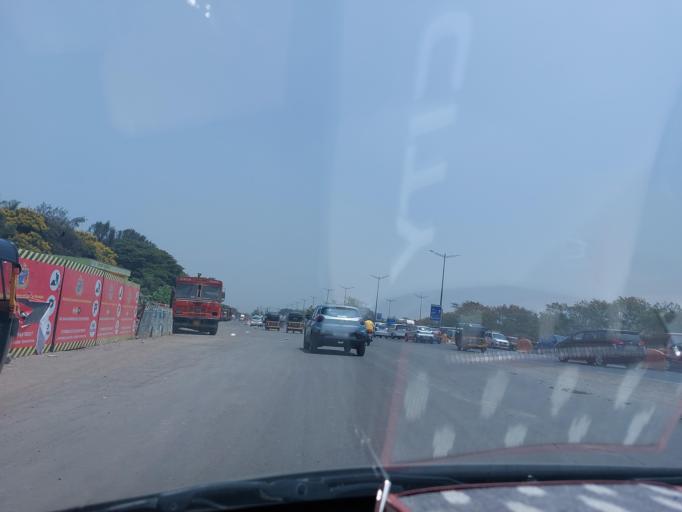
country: IN
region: Maharashtra
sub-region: Mumbai Suburban
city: Mumbai
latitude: 19.0798
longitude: 72.9170
